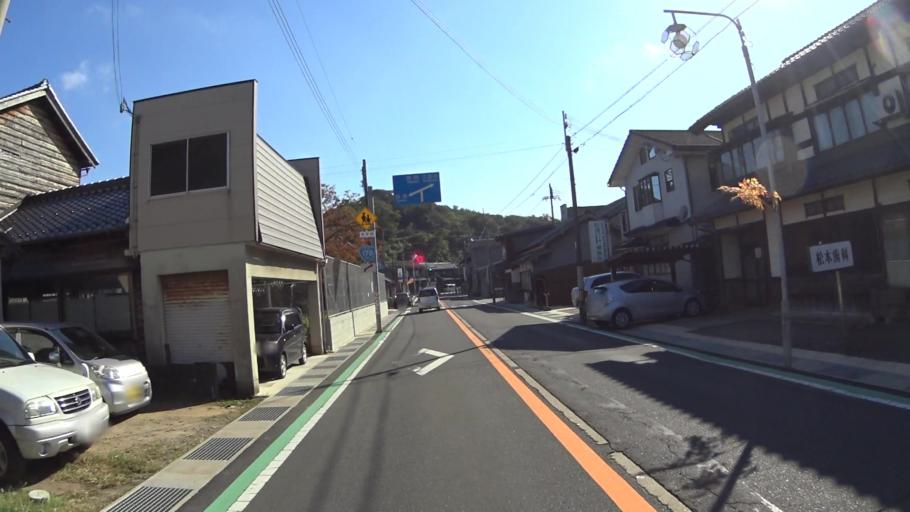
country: JP
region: Kyoto
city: Miyazu
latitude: 35.6809
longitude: 135.0303
